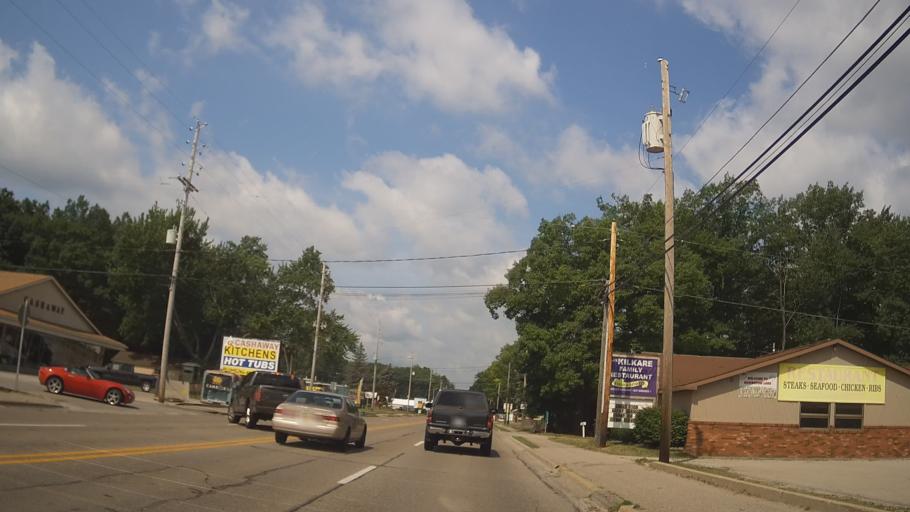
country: US
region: Michigan
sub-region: Roscommon County
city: Houghton Lake
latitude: 44.2985
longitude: -84.7170
